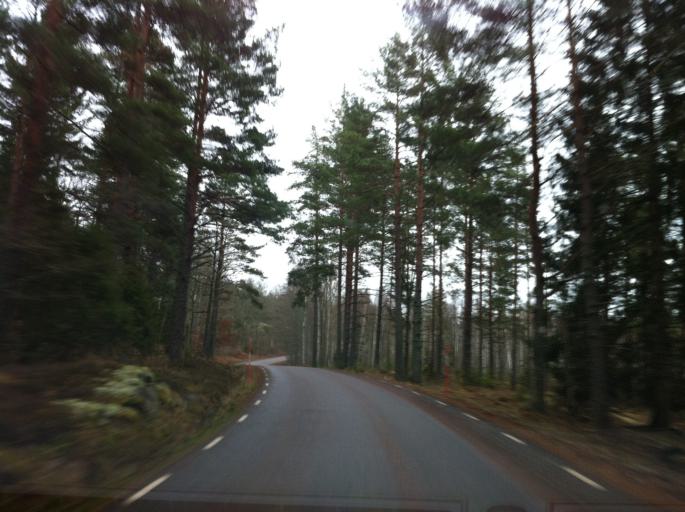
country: SE
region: Kalmar
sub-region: Vasterviks Kommun
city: Forserum
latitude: 57.9277
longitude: 16.5318
